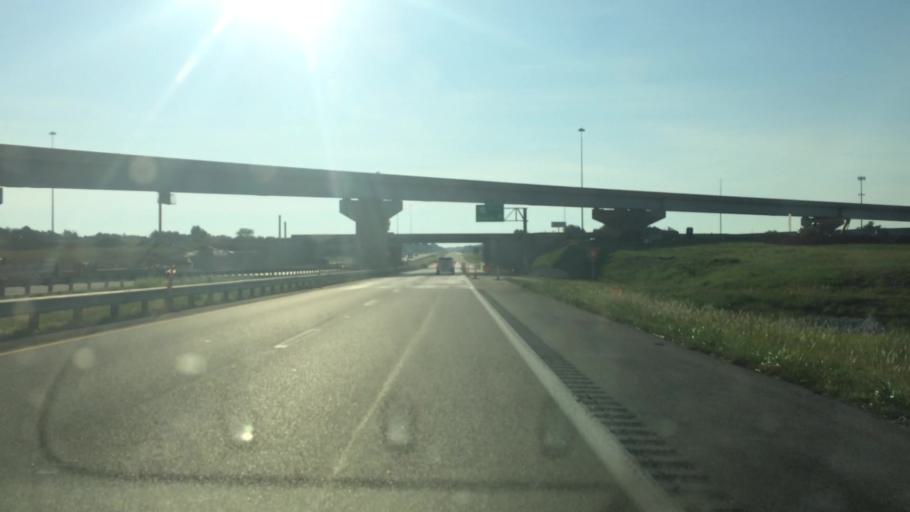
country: US
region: Missouri
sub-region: Greene County
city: Springfield
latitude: 37.2501
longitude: -93.2264
